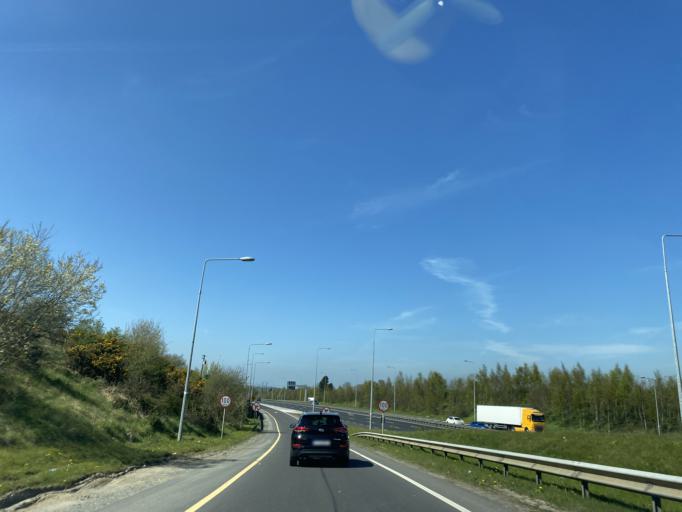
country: IE
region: Leinster
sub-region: Kildare
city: Kill
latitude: 53.2520
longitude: -6.5777
